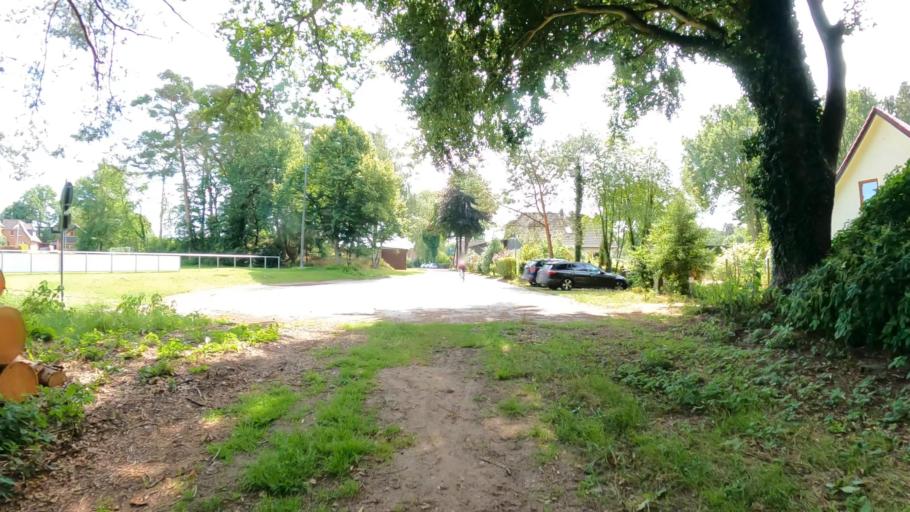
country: DE
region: Schleswig-Holstein
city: Wittenborn
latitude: 53.9280
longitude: 10.2209
